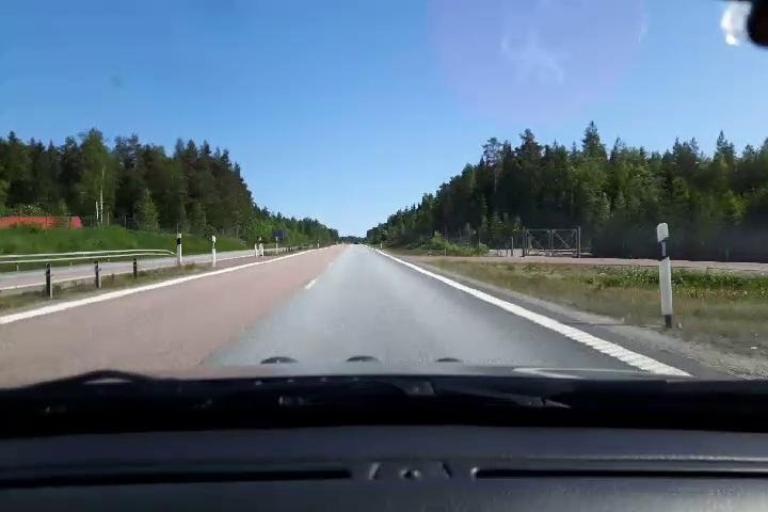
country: SE
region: Gaevleborg
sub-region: Soderhamns Kommun
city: Soderhamn
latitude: 61.3296
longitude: 17.0226
